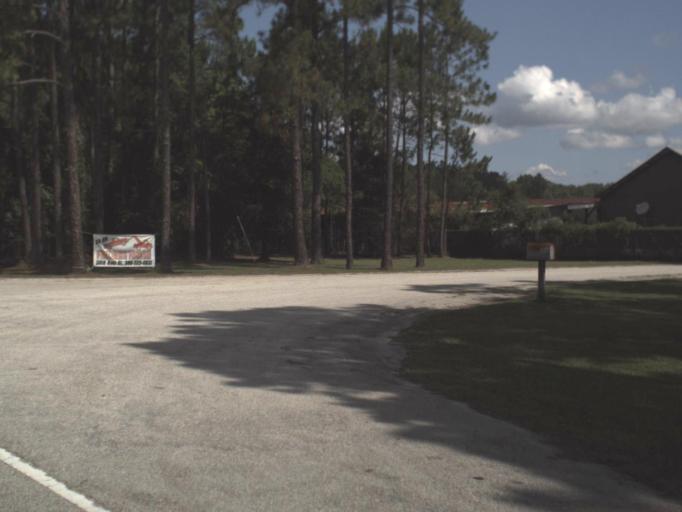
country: US
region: Florida
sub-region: Putnam County
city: Palatka
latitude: 29.6592
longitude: -81.6712
